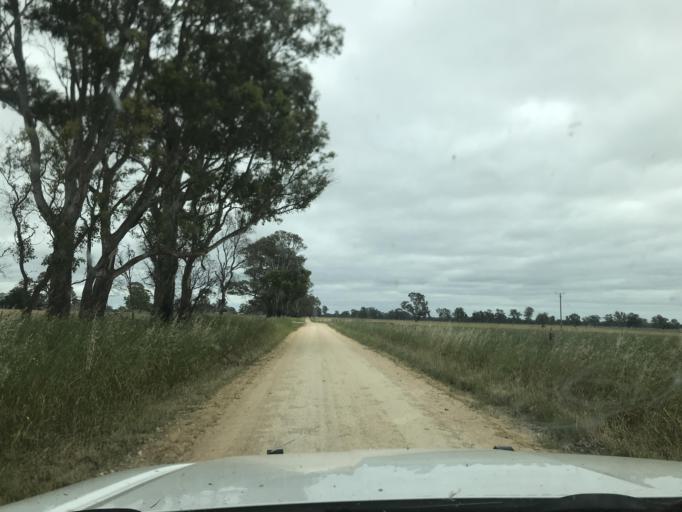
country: AU
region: South Australia
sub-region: Wattle Range
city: Penola
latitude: -37.1807
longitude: 141.0759
